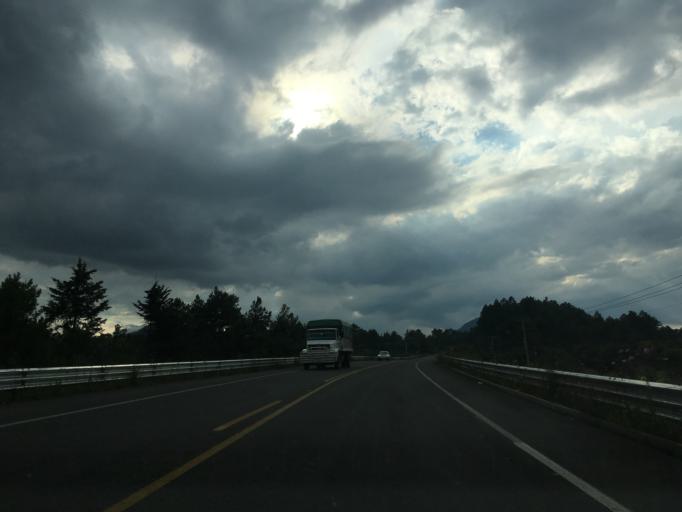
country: MX
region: Michoacan
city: Nuevo San Juan Parangaricutiro
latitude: 19.5046
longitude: -102.1309
